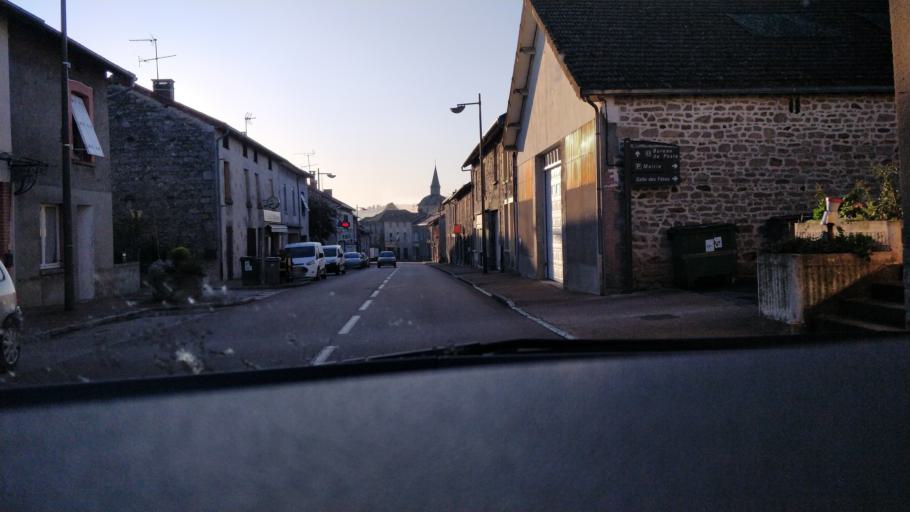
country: FR
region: Limousin
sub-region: Departement de la Haute-Vienne
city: Sauviat-sur-Vige
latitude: 45.9070
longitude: 1.6063
